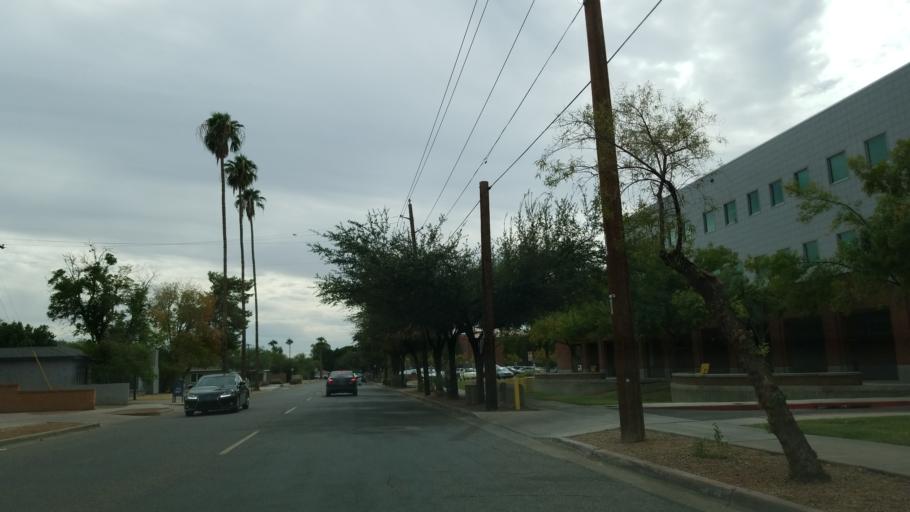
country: US
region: Arizona
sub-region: Maricopa County
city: Phoenix
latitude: 33.4831
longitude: -112.0870
